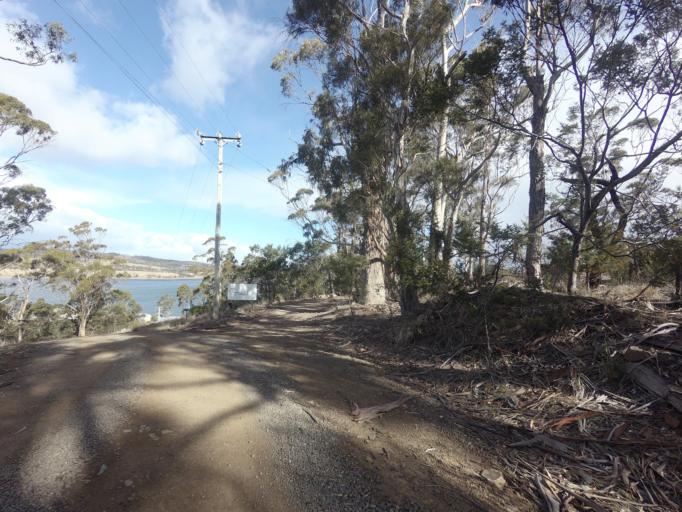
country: AU
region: Tasmania
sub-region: Sorell
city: Sorell
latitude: -42.3314
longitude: 147.9672
